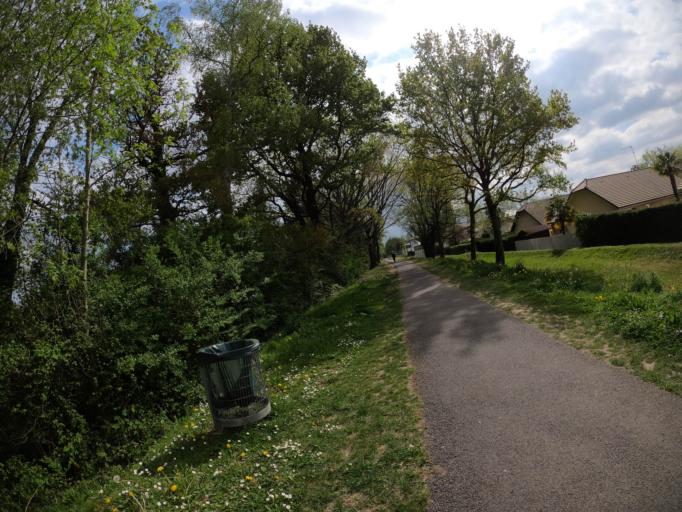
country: FR
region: Aquitaine
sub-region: Departement des Pyrenees-Atlantiques
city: Lons
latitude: 43.3215
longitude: -0.3851
